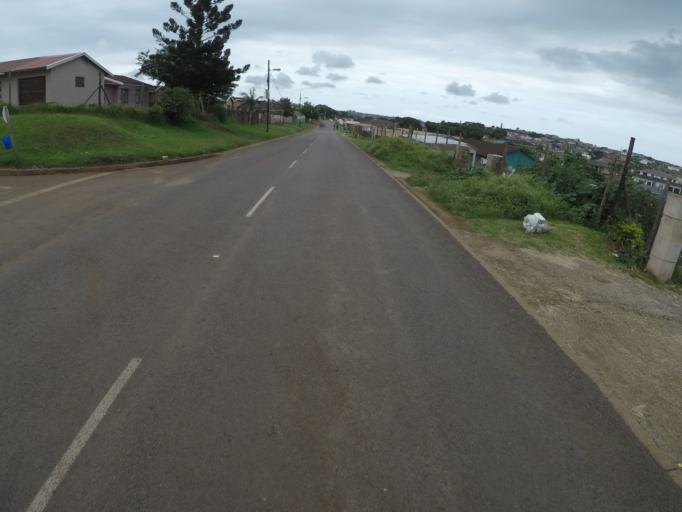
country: ZA
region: KwaZulu-Natal
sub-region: uThungulu District Municipality
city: Empangeni
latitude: -28.7774
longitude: 31.8483
